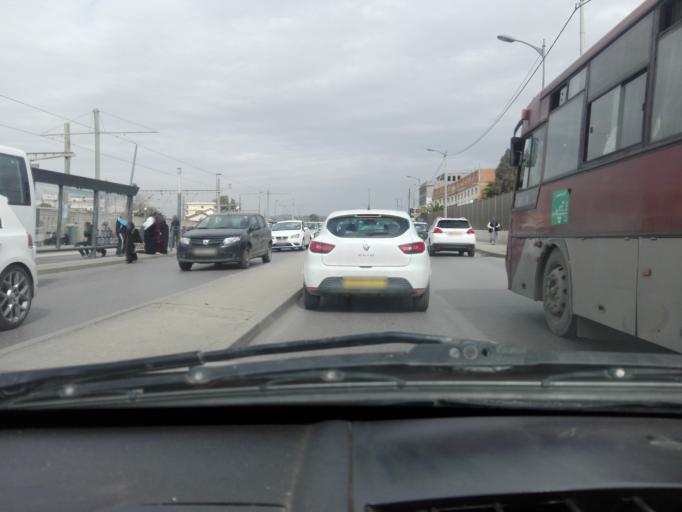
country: DZ
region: Alger
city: Bab Ezzouar
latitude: 36.7327
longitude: 3.1249
